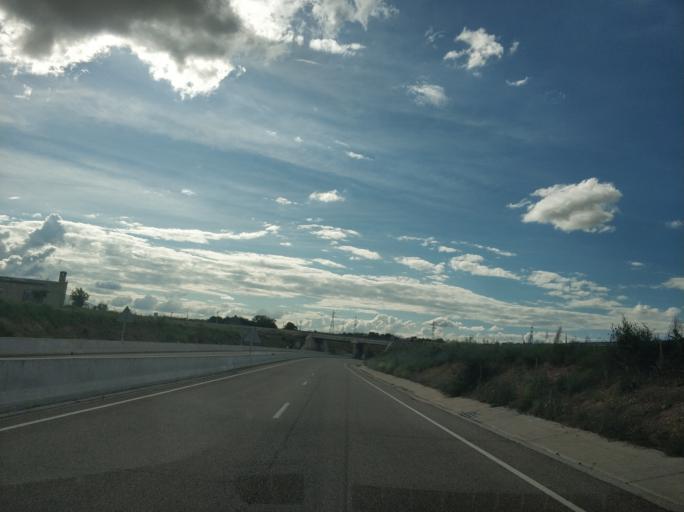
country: ES
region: Castille and Leon
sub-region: Provincia de Burgos
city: Aranda de Duero
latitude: 41.6927
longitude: -3.6708
